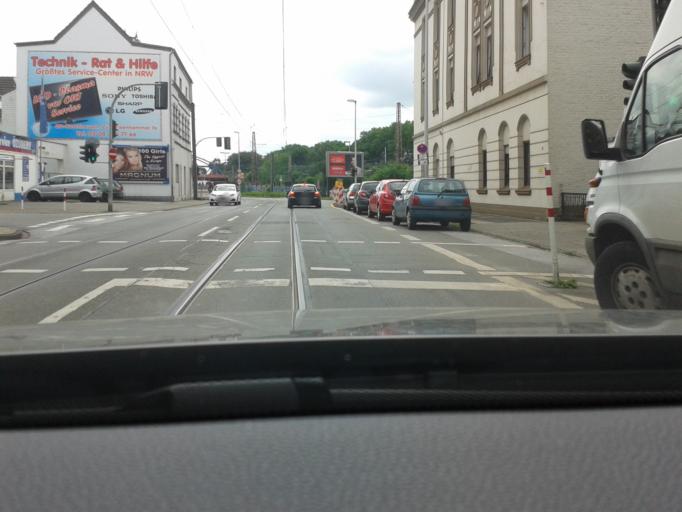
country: DE
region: North Rhine-Westphalia
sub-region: Regierungsbezirk Dusseldorf
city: Muelheim (Ruhr)
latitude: 51.4459
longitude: 6.8655
